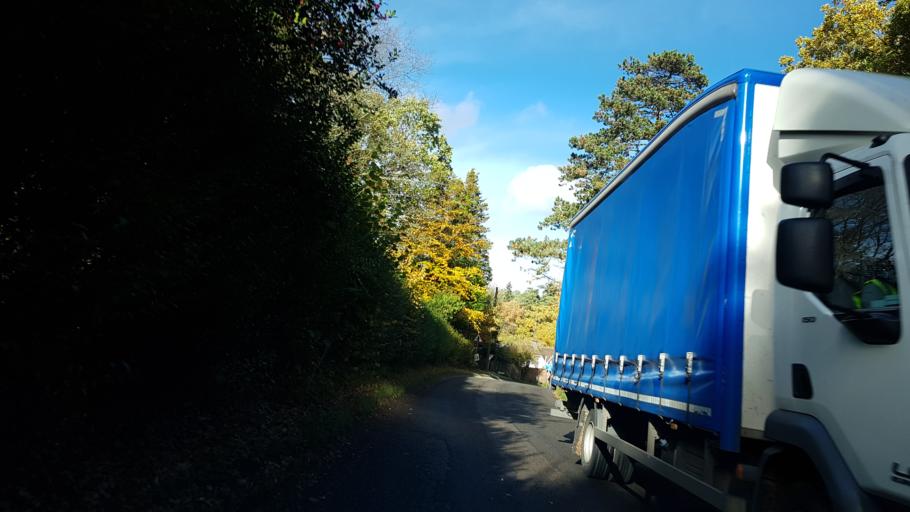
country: GB
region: England
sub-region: Surrey
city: Churt
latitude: 51.1446
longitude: -0.7556
